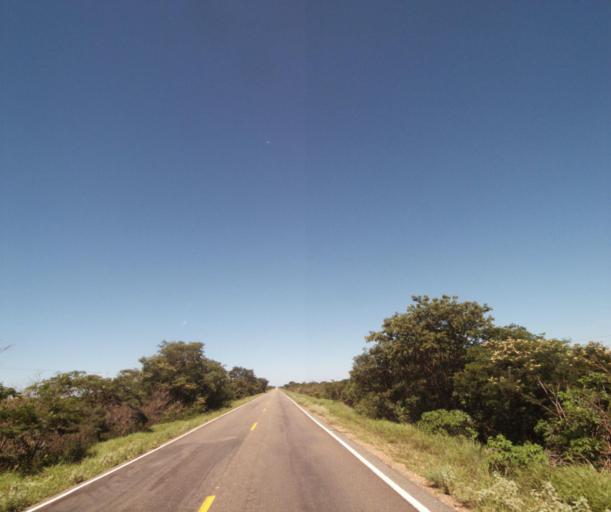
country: BR
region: Bahia
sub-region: Palmas De Monte Alto
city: Palmas de Monte Alto
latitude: -14.2668
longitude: -43.3737
